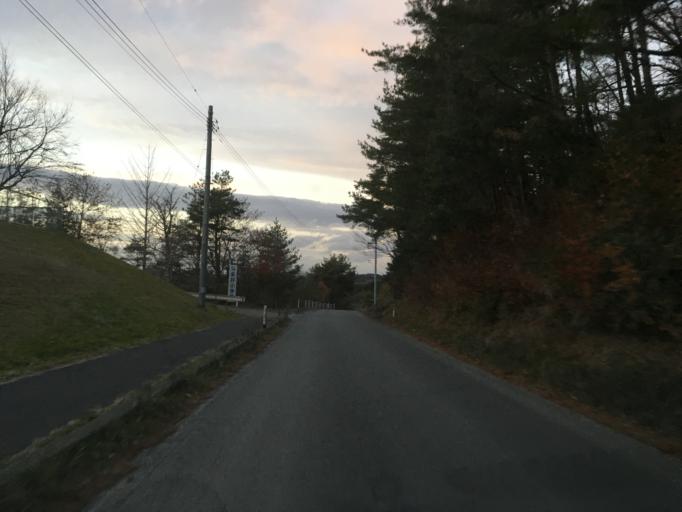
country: JP
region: Iwate
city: Ichinoseki
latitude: 38.7791
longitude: 141.2353
